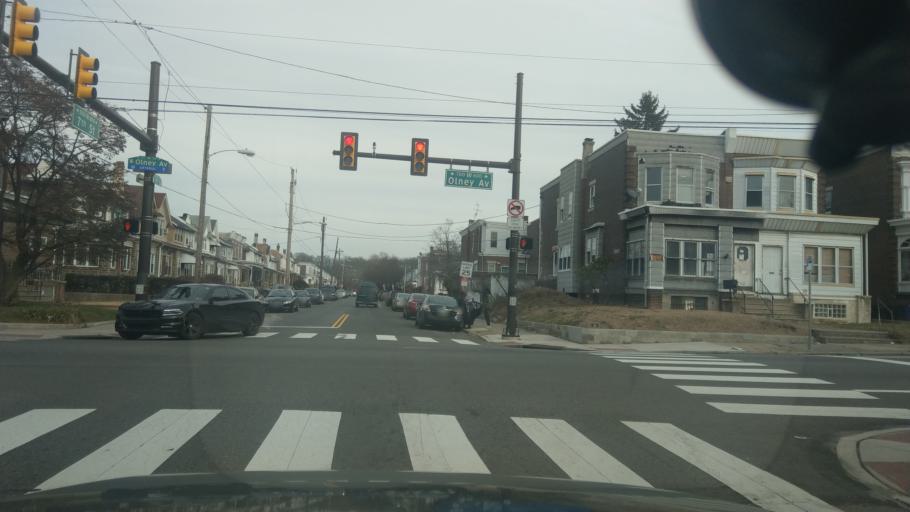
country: US
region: Pennsylvania
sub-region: Montgomery County
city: Wyncote
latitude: 40.0368
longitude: -75.1341
